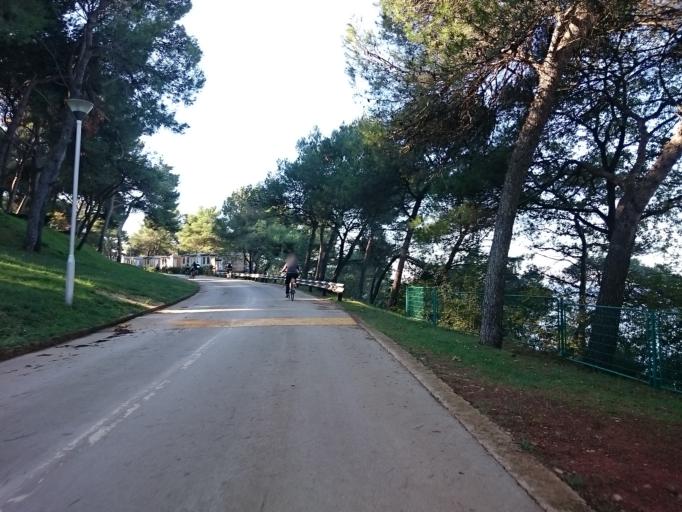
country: HR
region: Istarska
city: Novigrad
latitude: 45.3051
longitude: 13.5916
